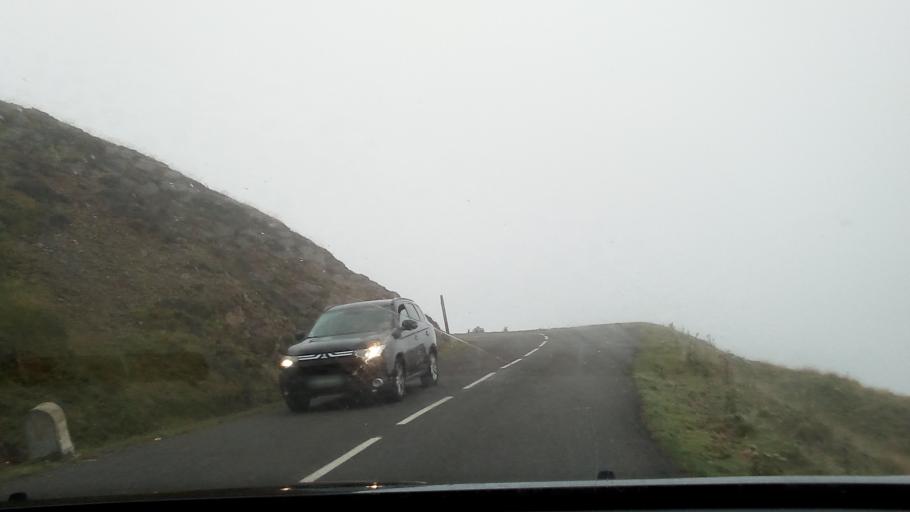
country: FR
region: Aquitaine
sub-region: Departement des Pyrenees-Atlantiques
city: Laruns
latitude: 42.9781
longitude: -0.3428
